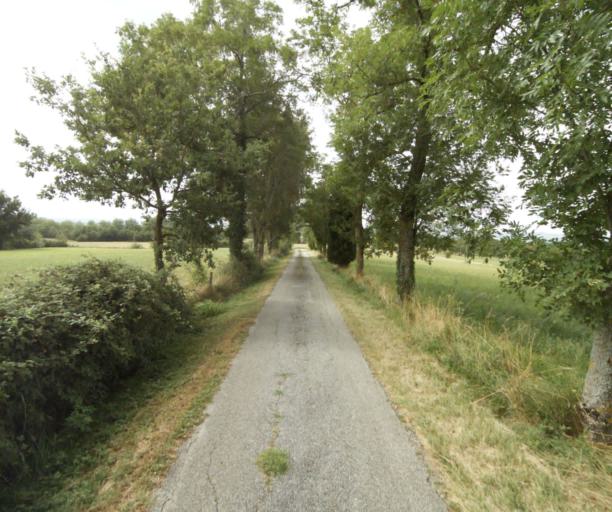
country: FR
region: Midi-Pyrenees
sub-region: Departement du Tarn
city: Soreze
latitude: 43.4605
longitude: 2.0839
